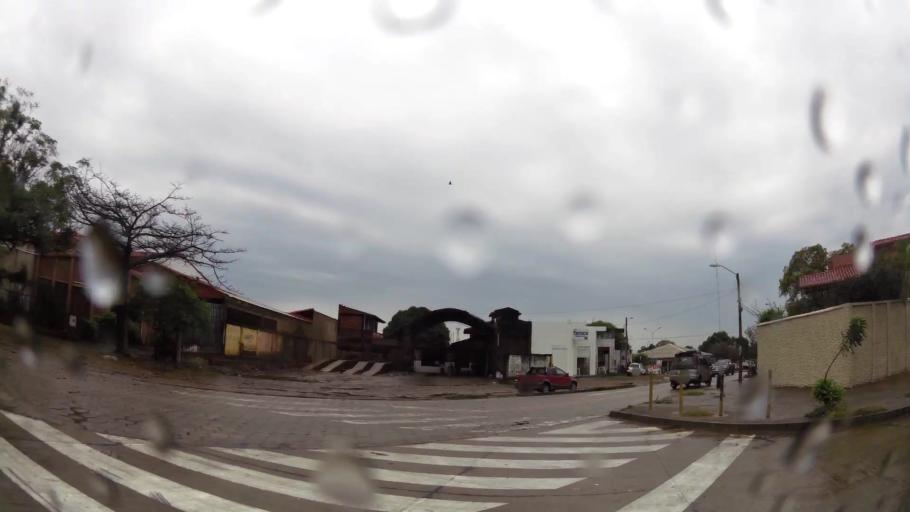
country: BO
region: Santa Cruz
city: Santa Cruz de la Sierra
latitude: -17.8164
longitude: -63.1992
